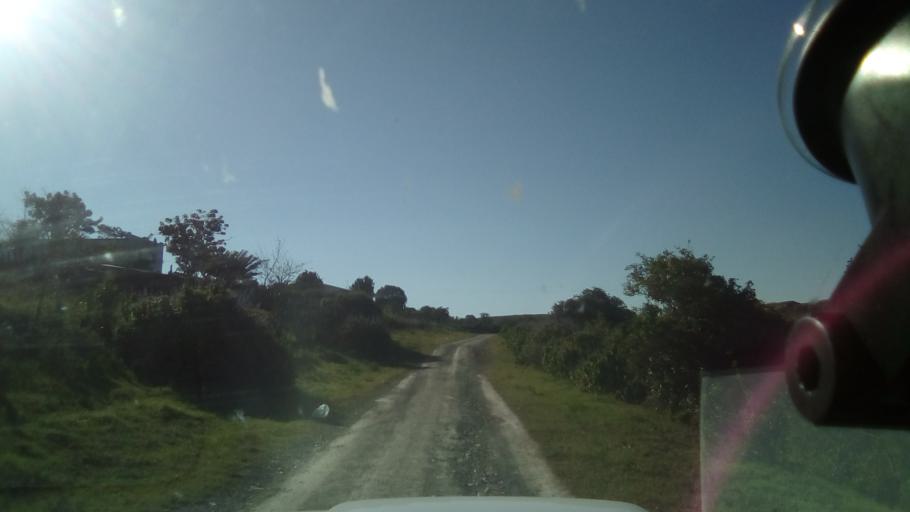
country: ZA
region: Eastern Cape
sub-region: Buffalo City Metropolitan Municipality
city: Bhisho
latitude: -32.8010
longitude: 27.3411
